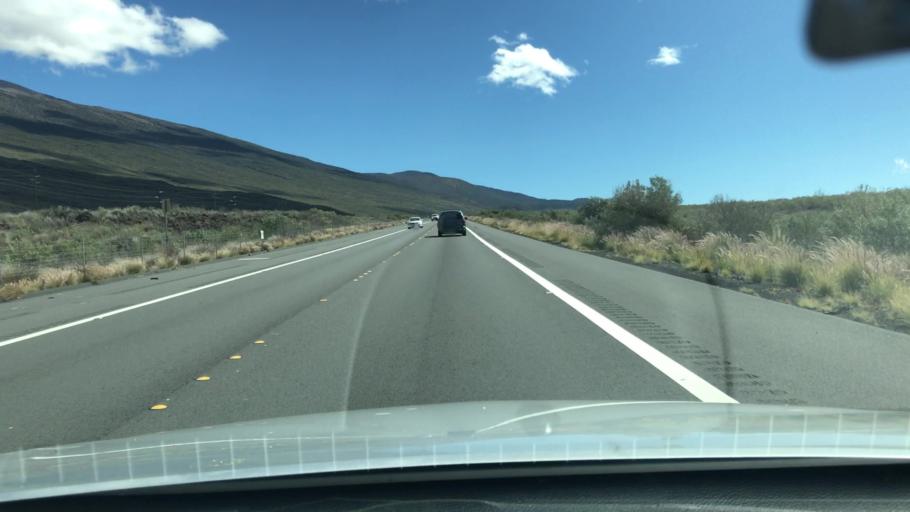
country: US
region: Hawaii
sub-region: Hawaii County
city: Waimea
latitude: 19.7649
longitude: -155.5638
